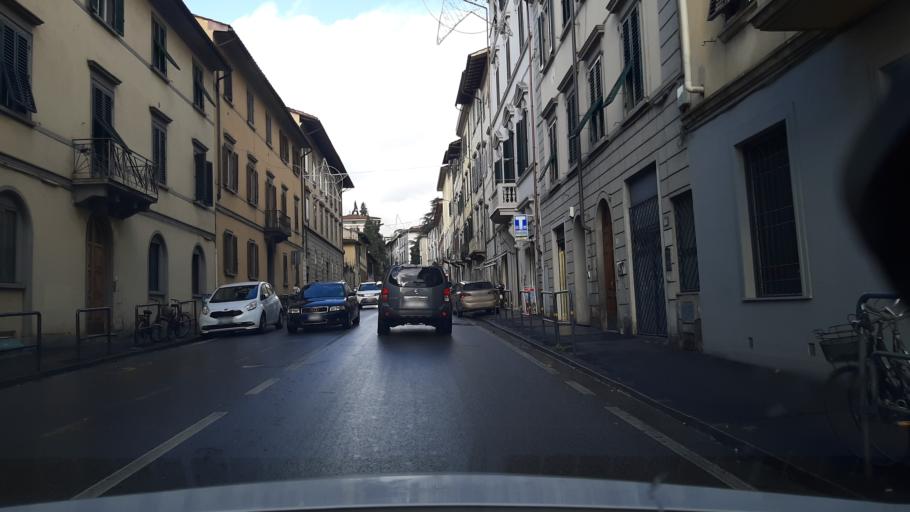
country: IT
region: Tuscany
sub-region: Province of Florence
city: Florence
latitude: 43.7866
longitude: 11.2624
